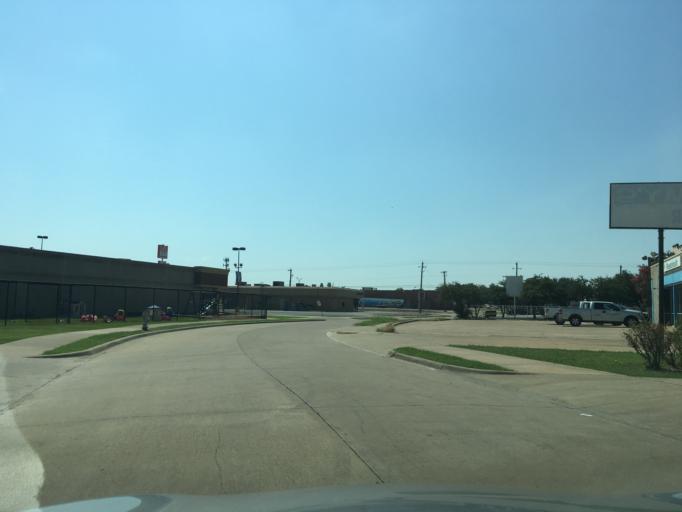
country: US
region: Texas
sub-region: Dallas County
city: Garland
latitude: 32.9322
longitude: -96.6517
